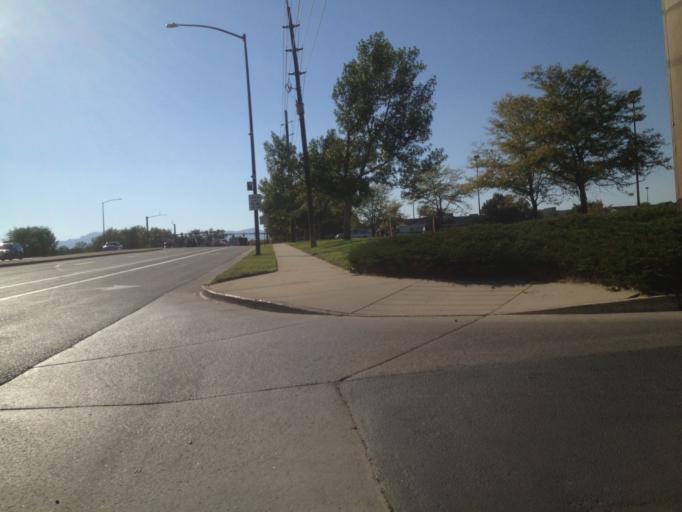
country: US
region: Colorado
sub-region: Boulder County
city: Louisville
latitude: 39.9870
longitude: -105.1254
